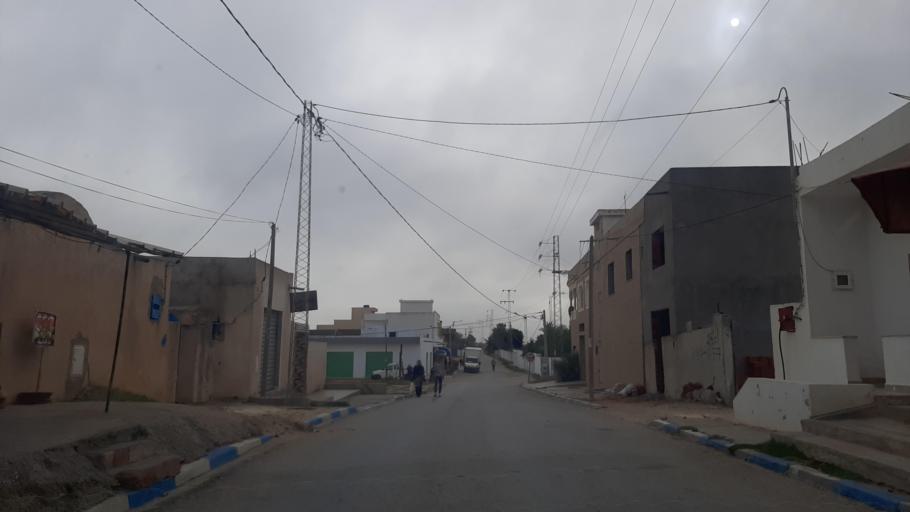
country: TN
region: Nabul
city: Menzel Heurr
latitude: 36.6797
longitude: 10.9250
